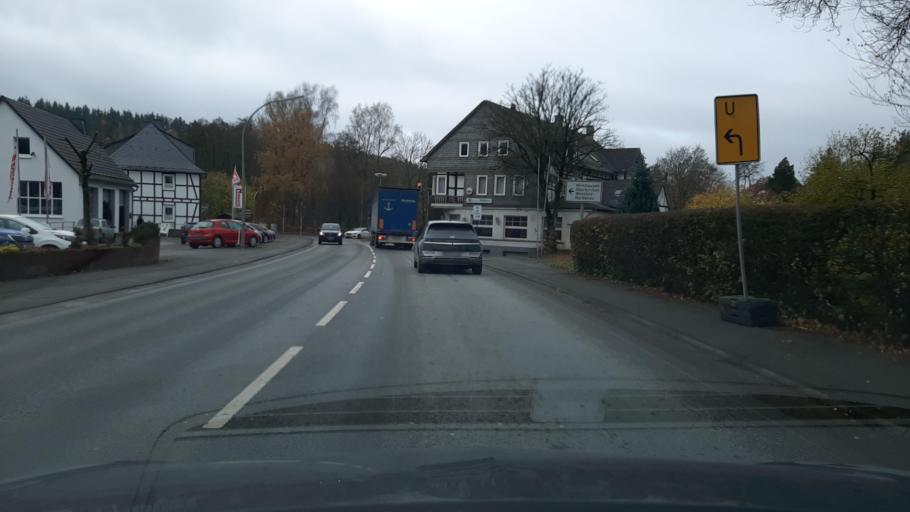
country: DE
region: North Rhine-Westphalia
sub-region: Regierungsbezirk Arnsberg
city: Bad Fredeburg
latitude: 51.1651
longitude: 8.3138
